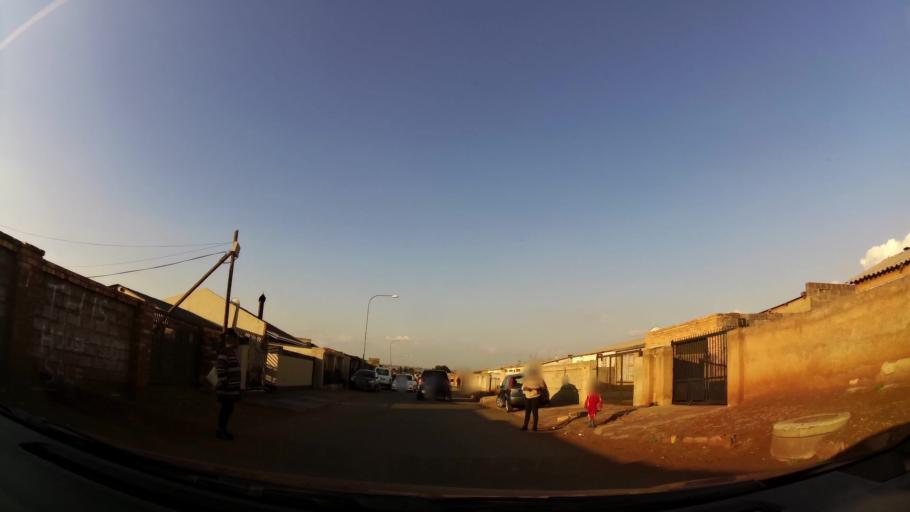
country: ZA
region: Gauteng
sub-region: City of Johannesburg Metropolitan Municipality
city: Soweto
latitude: -26.2255
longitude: 27.8550
